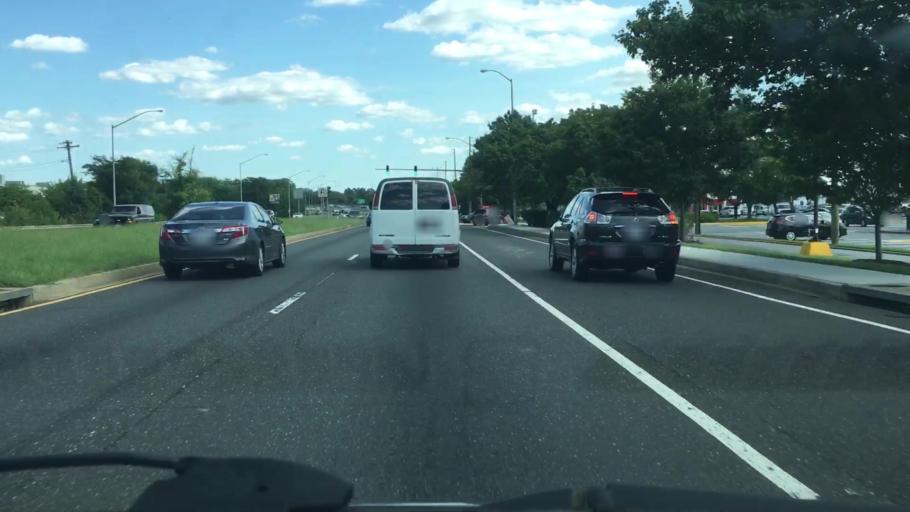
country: US
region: Maryland
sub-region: Prince George's County
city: Silver Hill
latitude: 38.8367
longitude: -76.9446
